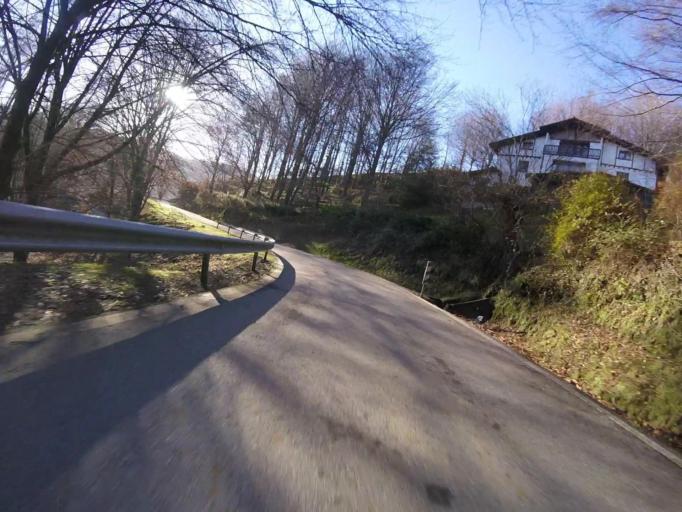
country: ES
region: Navarre
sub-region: Provincia de Navarra
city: Lesaka
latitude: 43.2672
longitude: -1.7615
